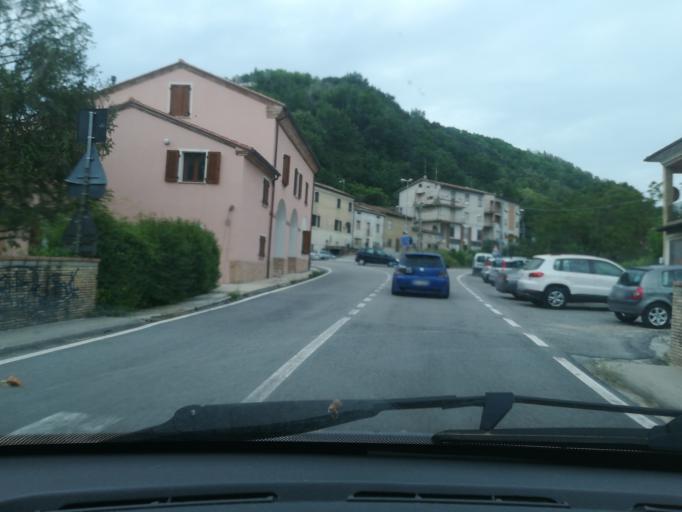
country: IT
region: The Marches
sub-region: Provincia di Macerata
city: Passo di Treia
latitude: 43.2828
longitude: 13.3339
